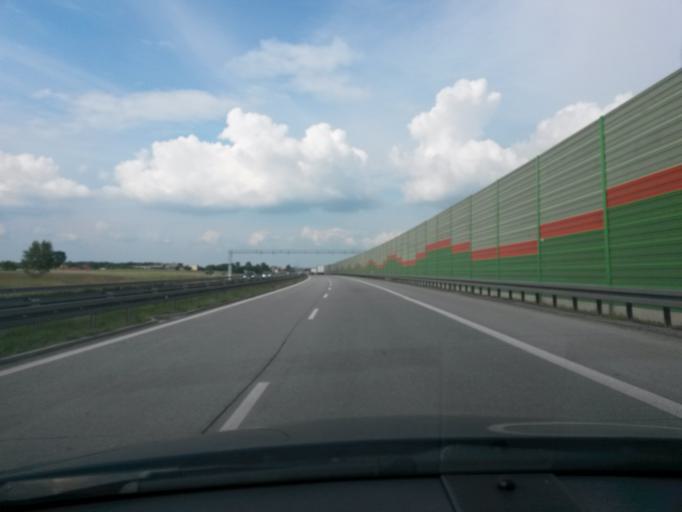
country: PL
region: Lodz Voivodeship
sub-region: Powiat tomaszowski
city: Lubochnia
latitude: 51.5979
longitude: 20.0561
